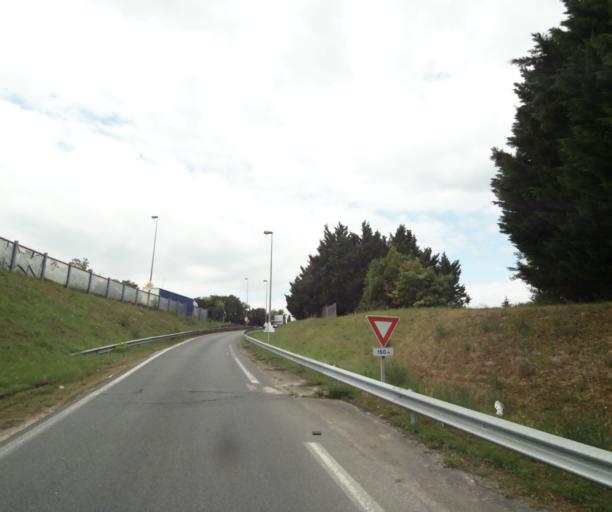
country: FR
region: Centre
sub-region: Departement du Loiret
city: Semoy
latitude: 47.9251
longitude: 1.9402
